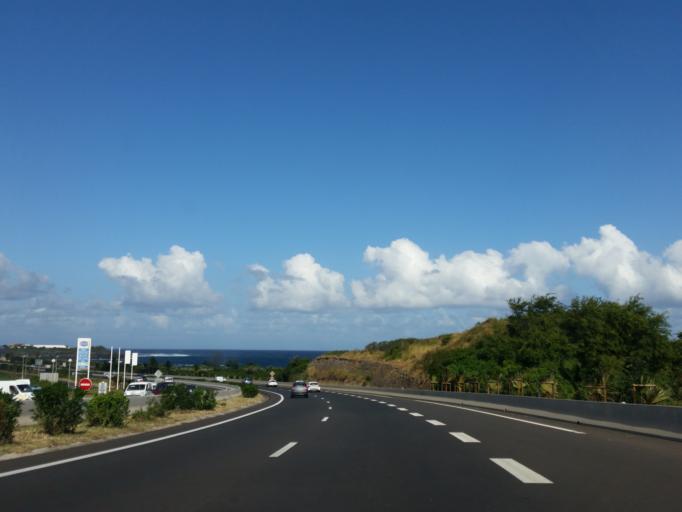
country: RE
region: Reunion
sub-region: Reunion
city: Saint-Pierre
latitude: -21.3232
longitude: 55.4463
